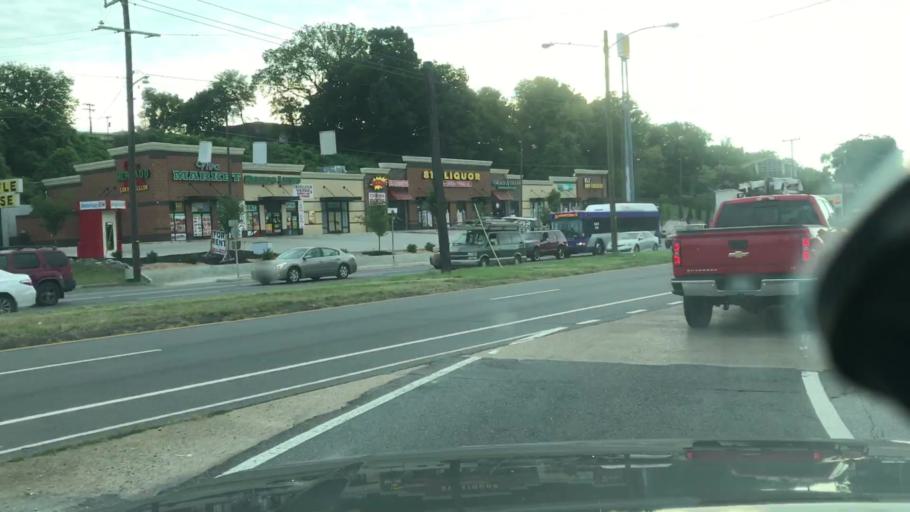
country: US
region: Tennessee
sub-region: Davidson County
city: Nashville
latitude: 36.1353
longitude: -86.7248
